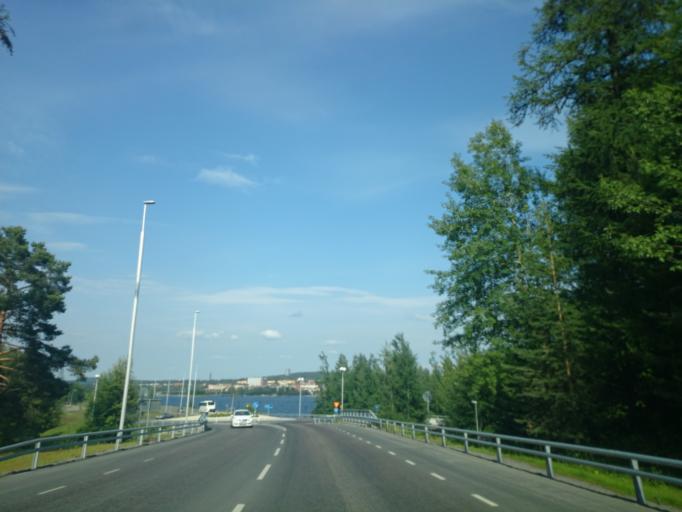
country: SE
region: Jaemtland
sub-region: OEstersunds Kommun
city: Ostersund
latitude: 63.1723
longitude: 14.6079
